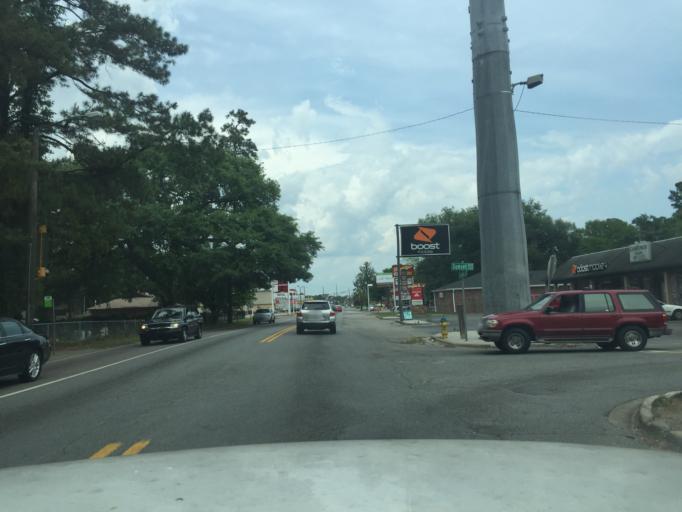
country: US
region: Georgia
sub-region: Chatham County
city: Thunderbolt
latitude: 32.0341
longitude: -81.0679
